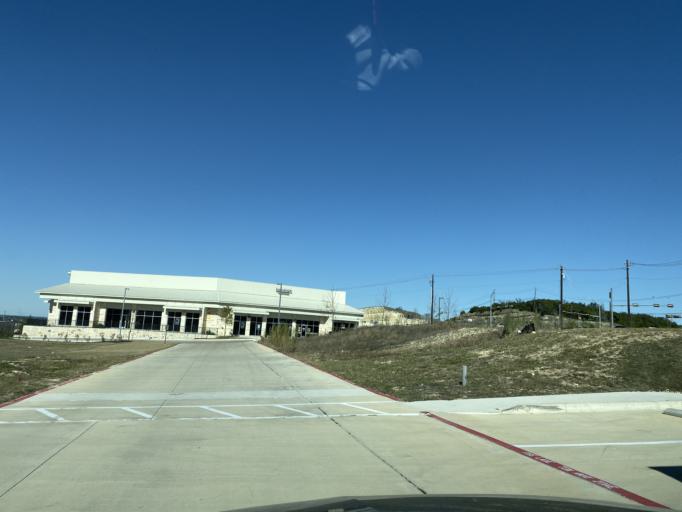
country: US
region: Texas
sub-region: Travis County
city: The Hills
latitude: 30.3333
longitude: -97.9694
